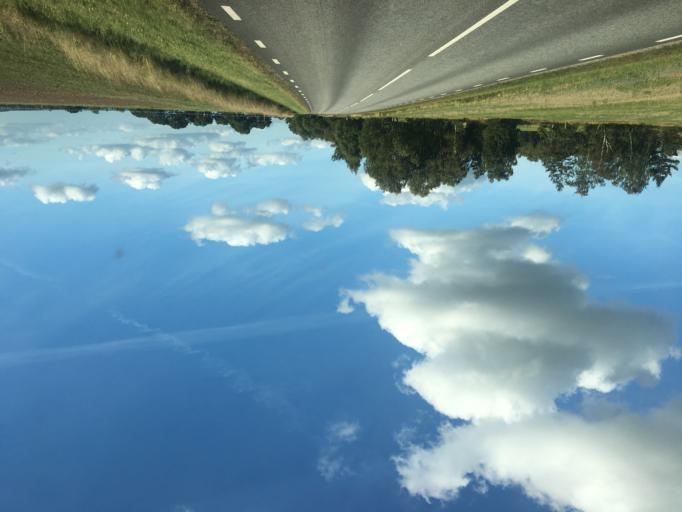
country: SE
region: Skane
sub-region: Hoors Kommun
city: Loberod
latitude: 55.7257
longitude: 13.4986
